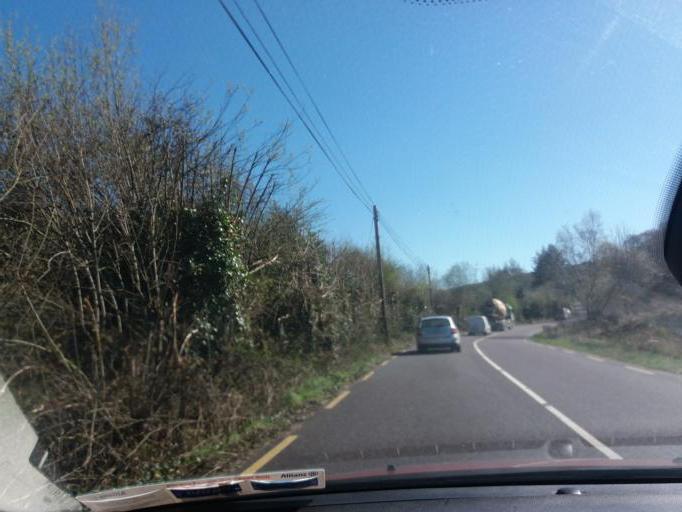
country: IE
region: Munster
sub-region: Ciarrai
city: Cill Airne
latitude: 51.9800
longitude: -9.3243
